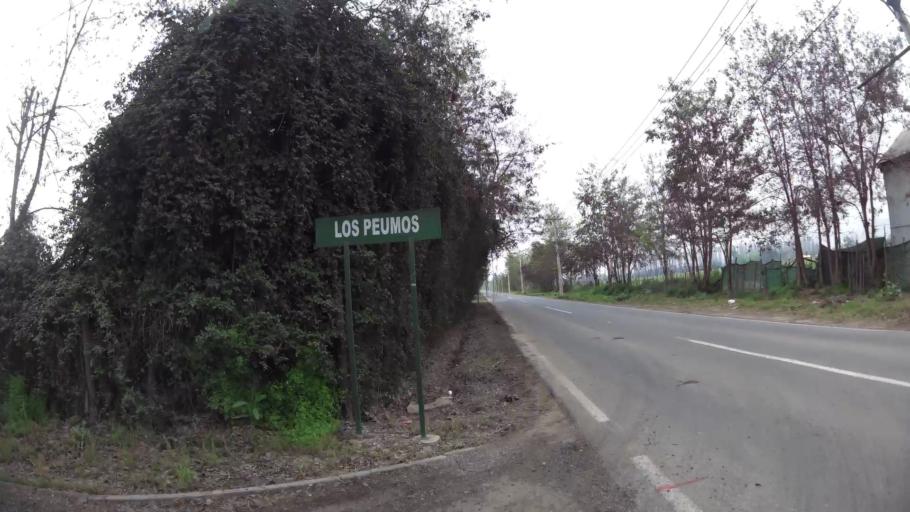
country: CL
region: Santiago Metropolitan
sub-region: Provincia de Chacabuco
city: Chicureo Abajo
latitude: -33.2571
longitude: -70.7094
